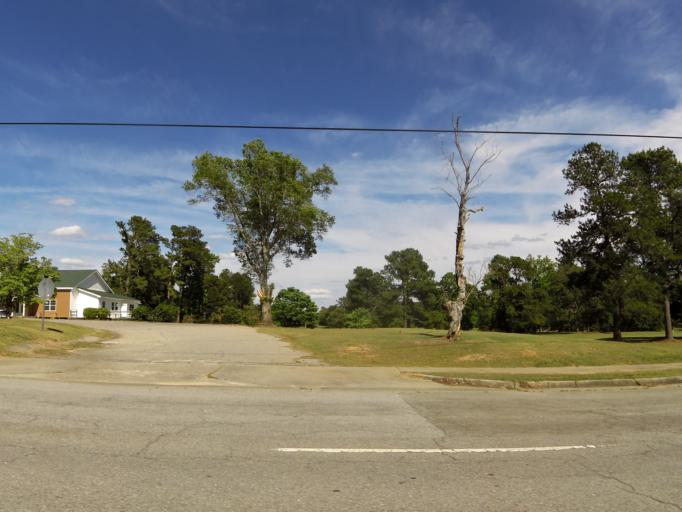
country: US
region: South Carolina
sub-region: Bamberg County
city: Denmark
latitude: 33.3001
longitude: -81.1456
